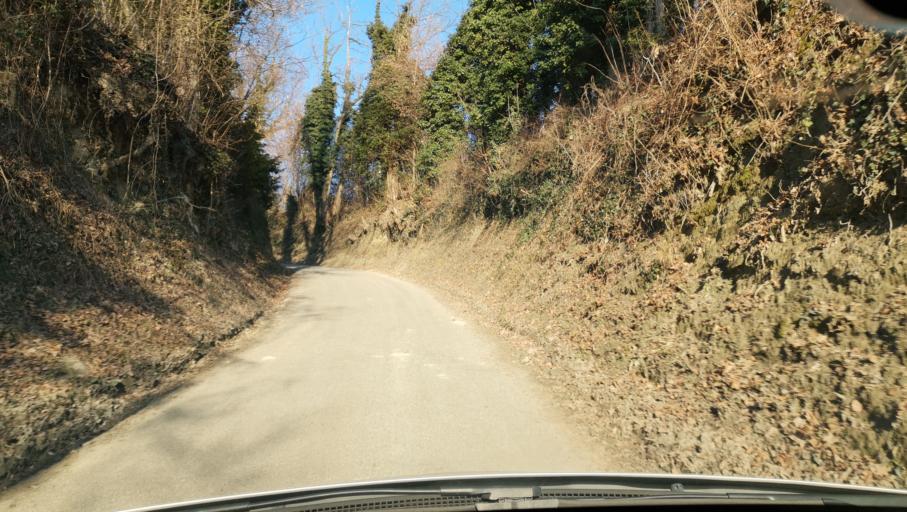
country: IT
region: Piedmont
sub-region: Provincia di Torino
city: San Raffaele Cimena
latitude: 45.1381
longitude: 7.8650
